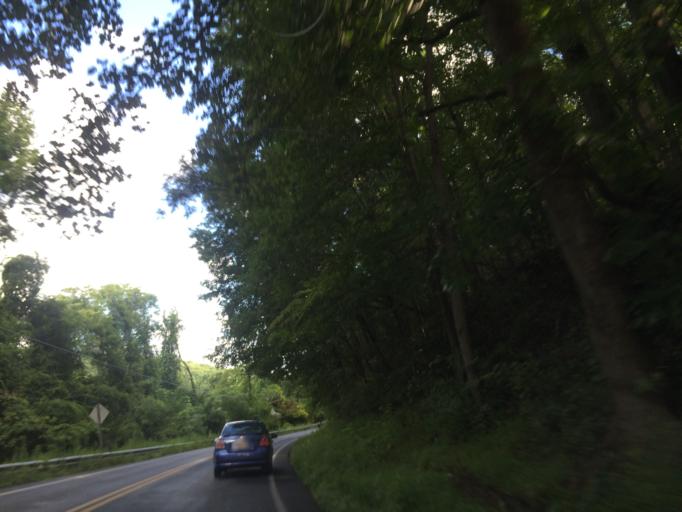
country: US
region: Maryland
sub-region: Carroll County
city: Sykesville
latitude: 39.3382
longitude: -76.9056
